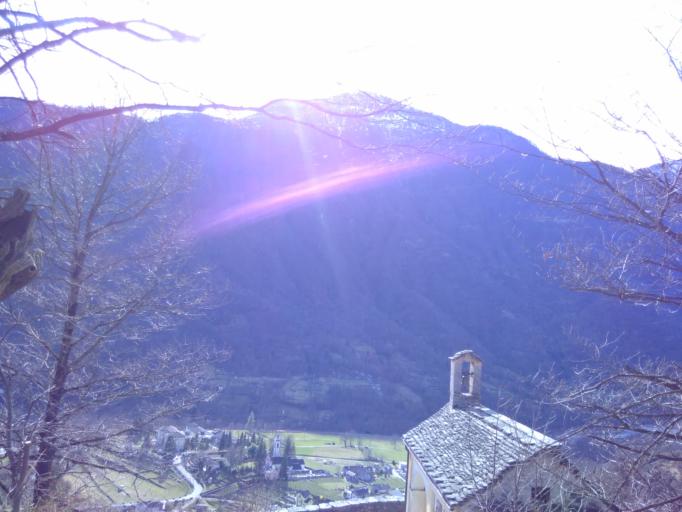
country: CH
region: Ticino
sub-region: Locarno District
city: Verscio
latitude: 46.2511
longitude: 8.7086
